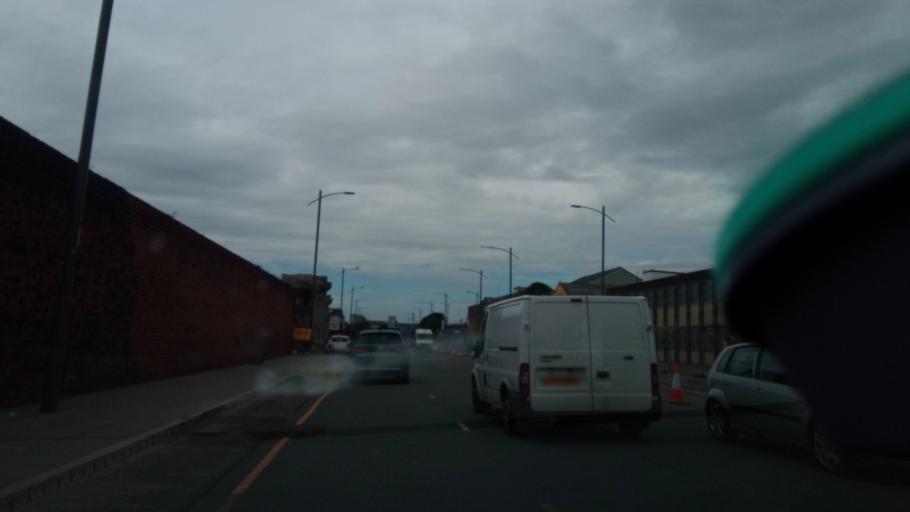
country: GB
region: England
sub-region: Liverpool
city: Liverpool
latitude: 53.4217
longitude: -2.9967
